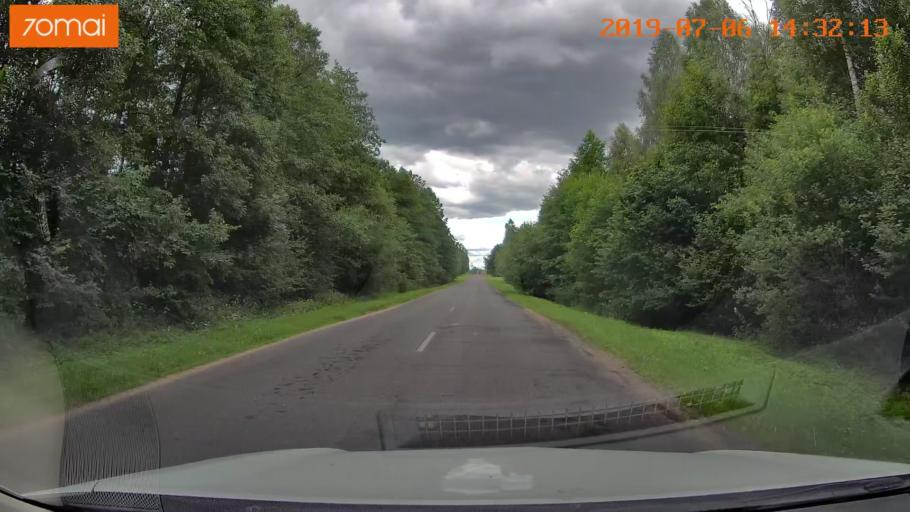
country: BY
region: Minsk
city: Ivyanyets
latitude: 53.9094
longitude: 26.7638
